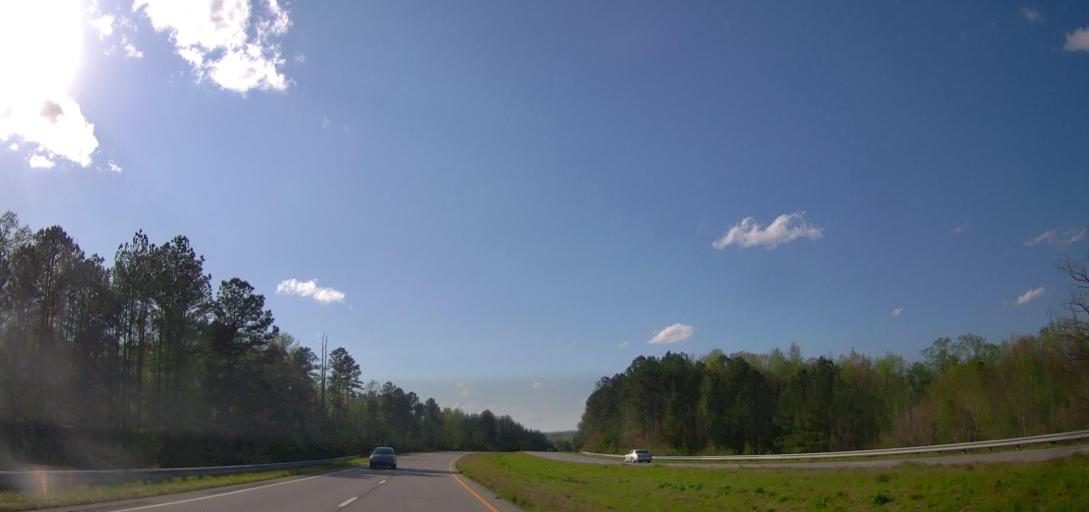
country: US
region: Georgia
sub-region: Baldwin County
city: Hardwick
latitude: 33.0268
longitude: -83.2429
